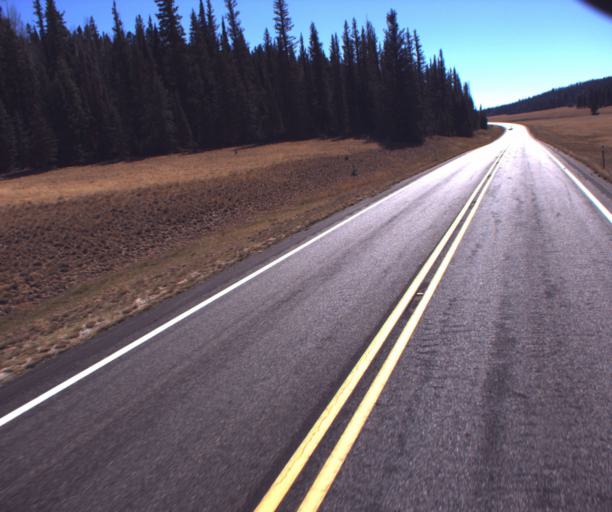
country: US
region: Arizona
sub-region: Coconino County
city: Grand Canyon
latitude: 36.3808
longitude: -112.1261
